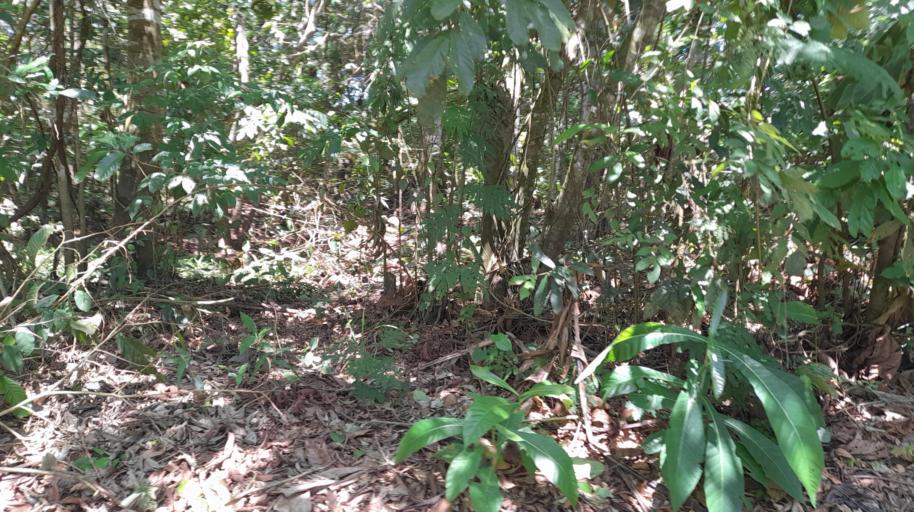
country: PE
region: Ucayali
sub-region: Provincia de Coronel Portillo
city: Puerto Callao
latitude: -8.2645
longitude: -74.6400
